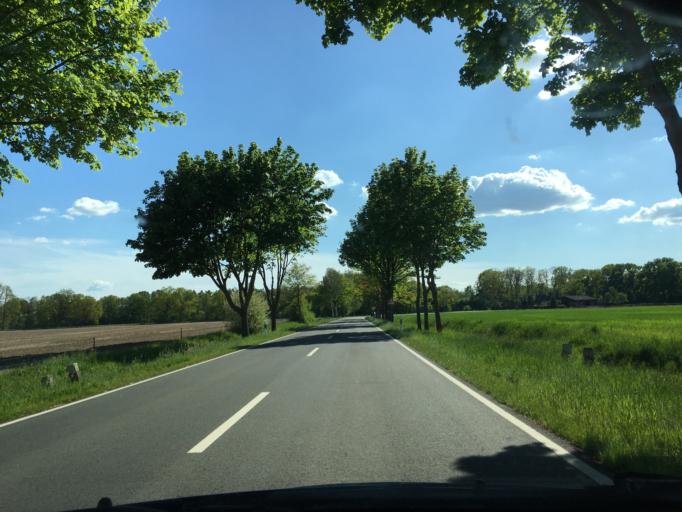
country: DE
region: Brandenburg
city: Lanz
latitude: 53.0176
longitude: 11.5519
